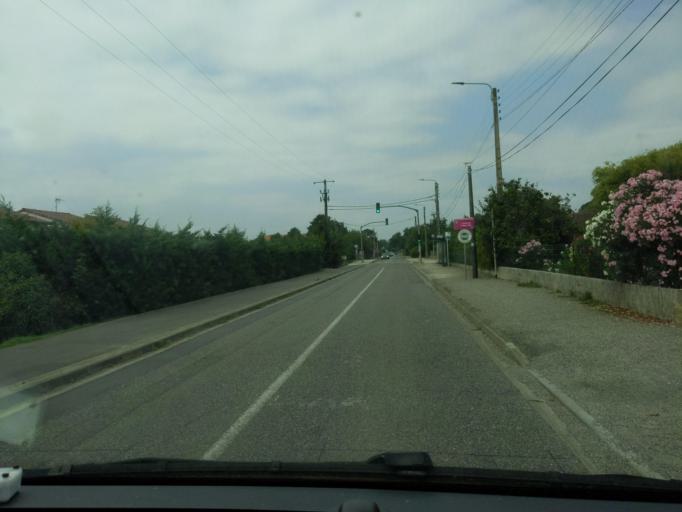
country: FR
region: Midi-Pyrenees
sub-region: Departement de la Haute-Garonne
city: Labege
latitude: 43.5275
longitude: 1.5385
